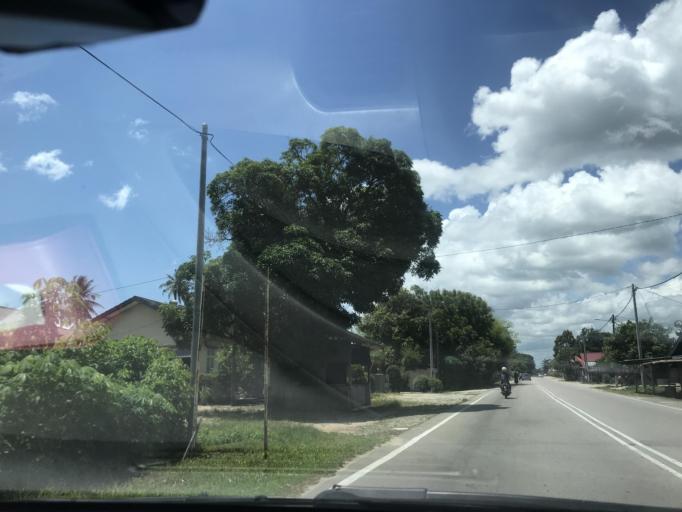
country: MY
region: Kelantan
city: Tumpat
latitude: 6.1932
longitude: 102.1496
